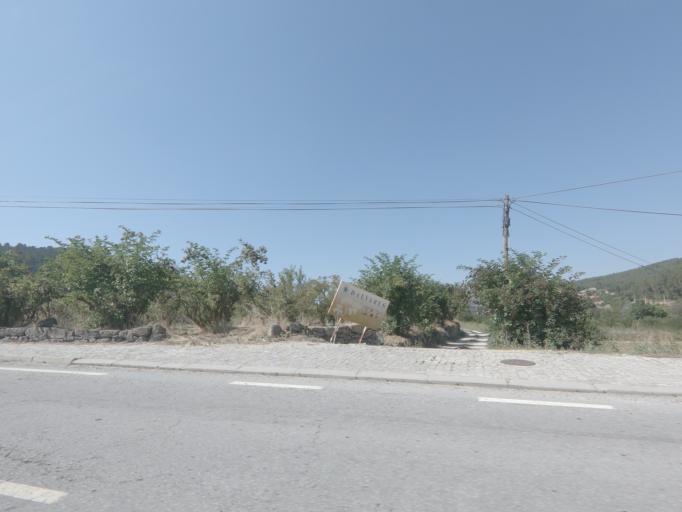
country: PT
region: Viseu
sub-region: Tarouca
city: Tarouca
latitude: 41.0287
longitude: -7.7574
